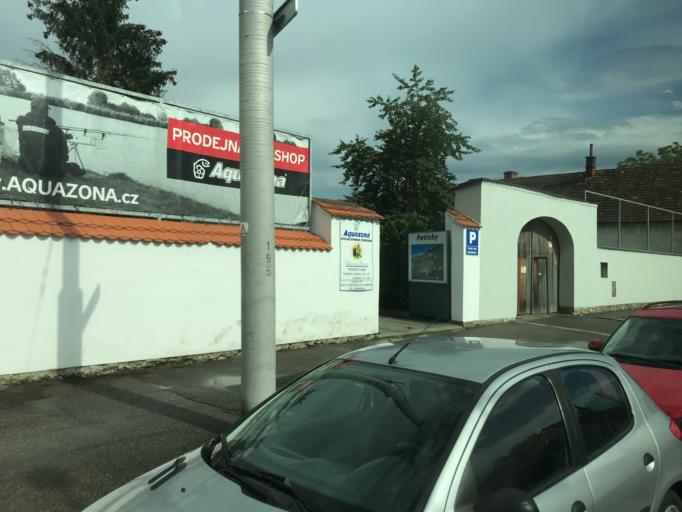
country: CZ
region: Jihocesky
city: Litvinovice
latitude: 48.9477
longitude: 14.4651
